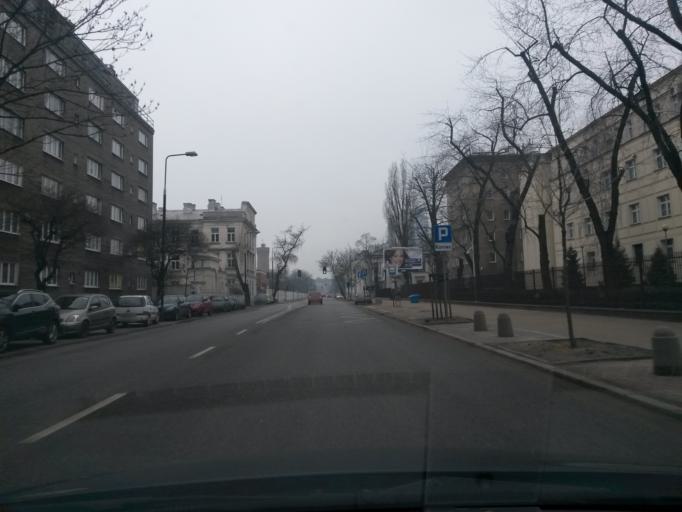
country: PL
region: Masovian Voivodeship
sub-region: Warszawa
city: Warsaw
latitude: 52.2232
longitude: 21.0020
